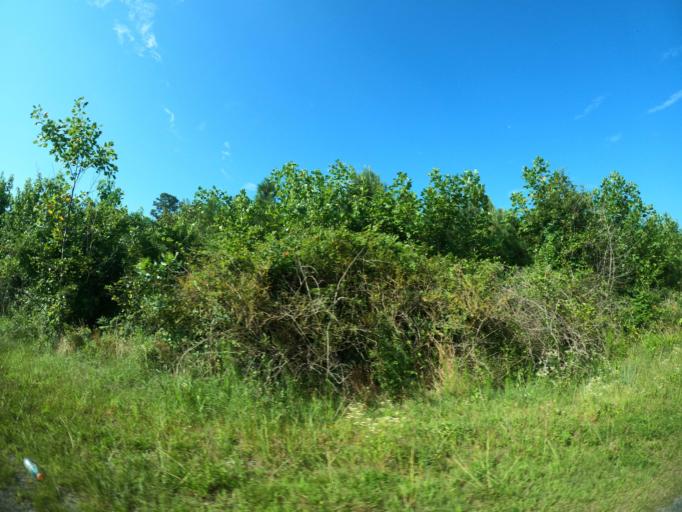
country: US
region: Delaware
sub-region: Sussex County
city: Ocean View
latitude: 38.4921
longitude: -75.1263
